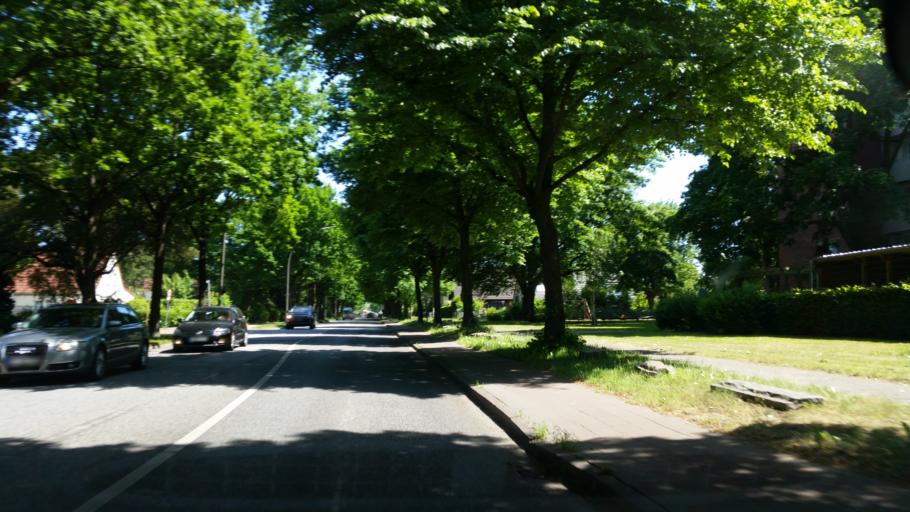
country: DE
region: Hamburg
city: Wandsbek
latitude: 53.5502
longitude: 10.1062
